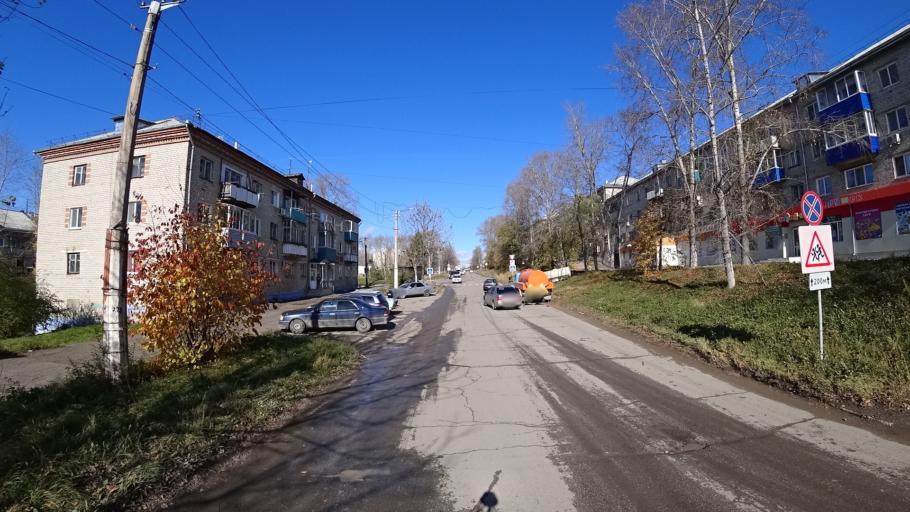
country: RU
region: Khabarovsk Krai
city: Amursk
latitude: 50.2180
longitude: 136.9032
